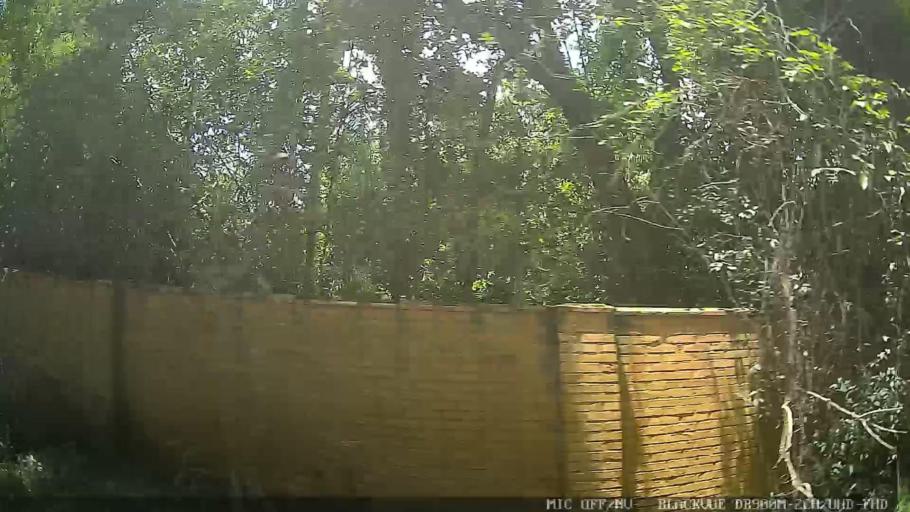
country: BR
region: Sao Paulo
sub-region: Jarinu
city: Jarinu
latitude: -23.0948
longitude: -46.6429
